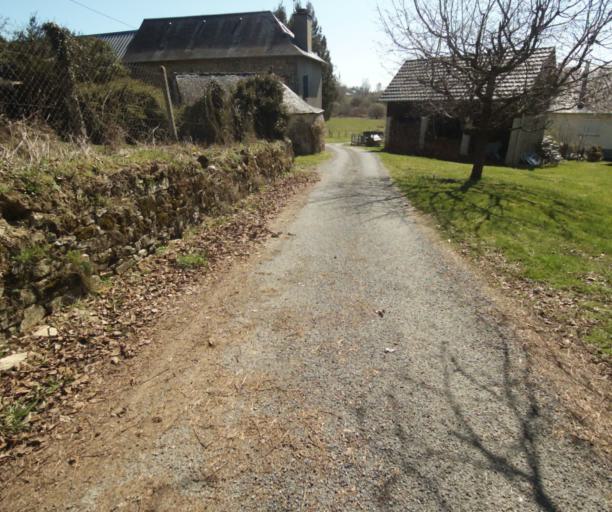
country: FR
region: Limousin
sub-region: Departement de la Correze
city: Saint-Mexant
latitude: 45.2775
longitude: 1.6754
